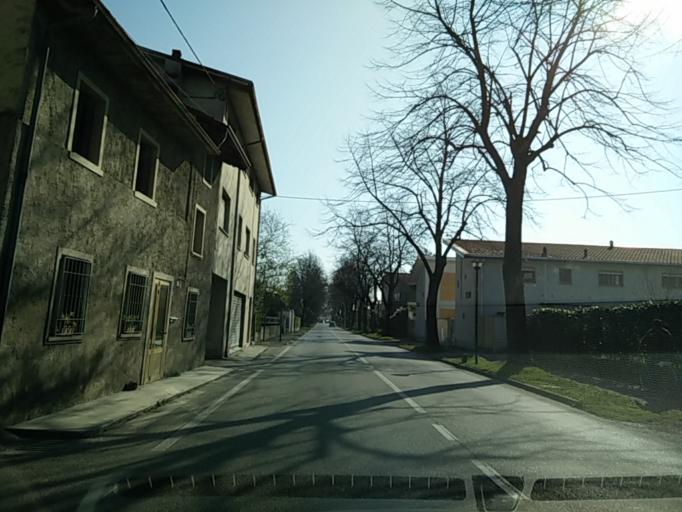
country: IT
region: Friuli Venezia Giulia
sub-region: Provincia di Pordenone
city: San Vito al Tagliamento
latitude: 45.9178
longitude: 12.8597
